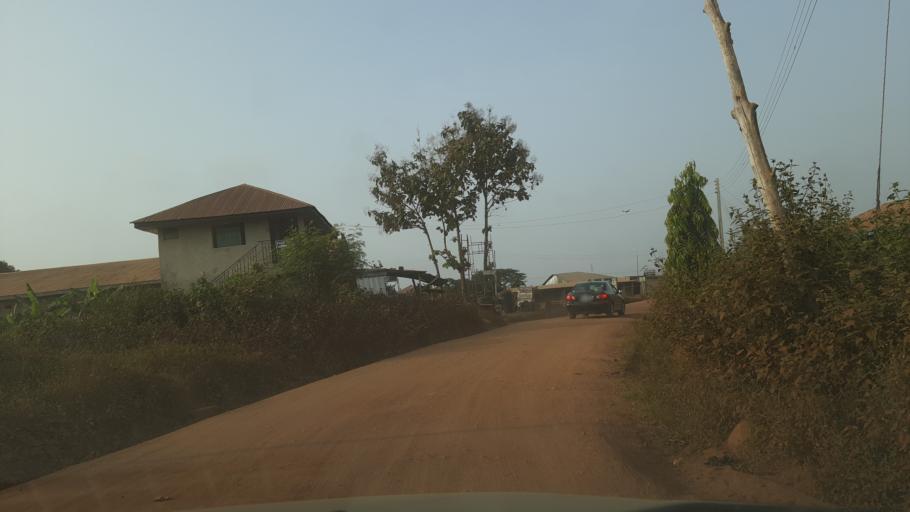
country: NG
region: Osun
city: Ilobu
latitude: 7.7926
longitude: 4.5008
